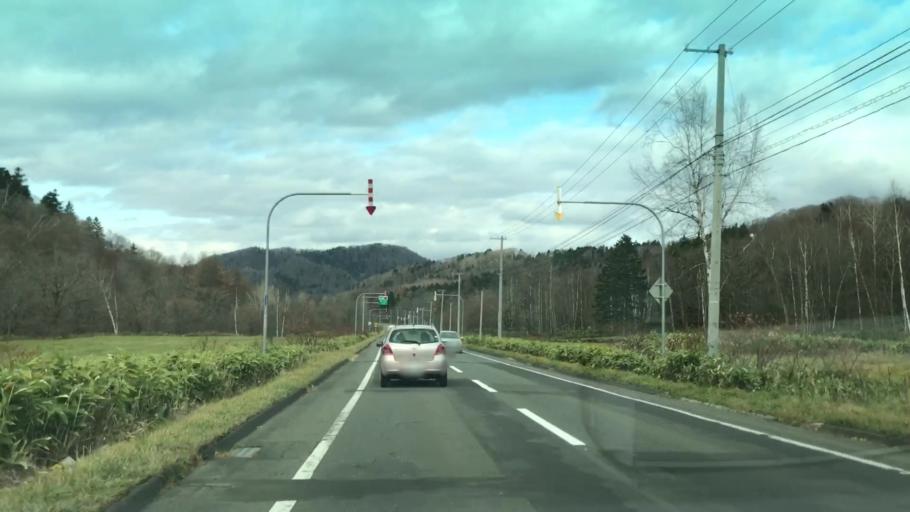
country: JP
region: Hokkaido
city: Shimo-furano
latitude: 42.9342
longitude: 142.4449
